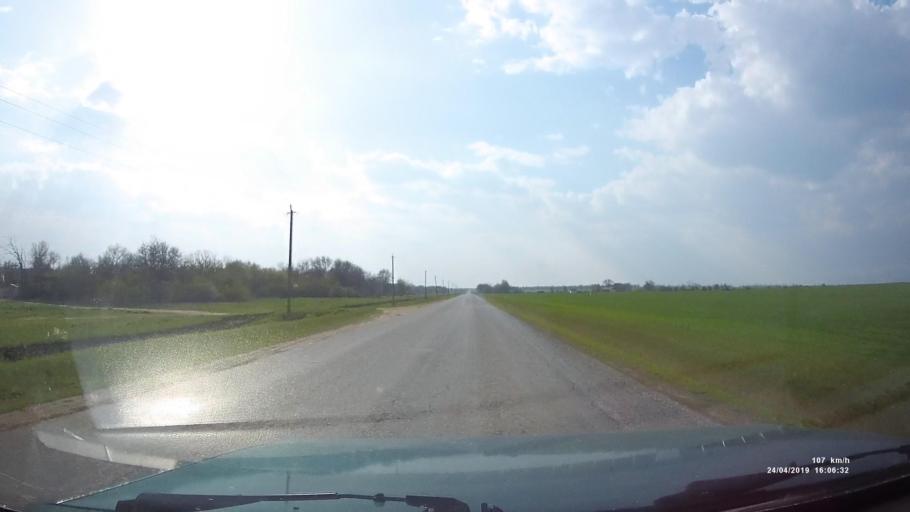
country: RU
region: Rostov
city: Sovetskoye
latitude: 46.6870
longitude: 42.3472
